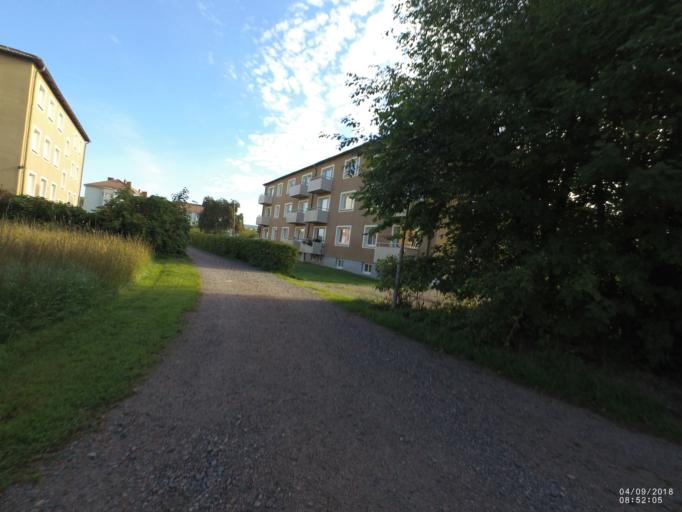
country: SE
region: Soedermanland
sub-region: Nykopings Kommun
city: Nykoping
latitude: 58.7538
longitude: 16.9858
